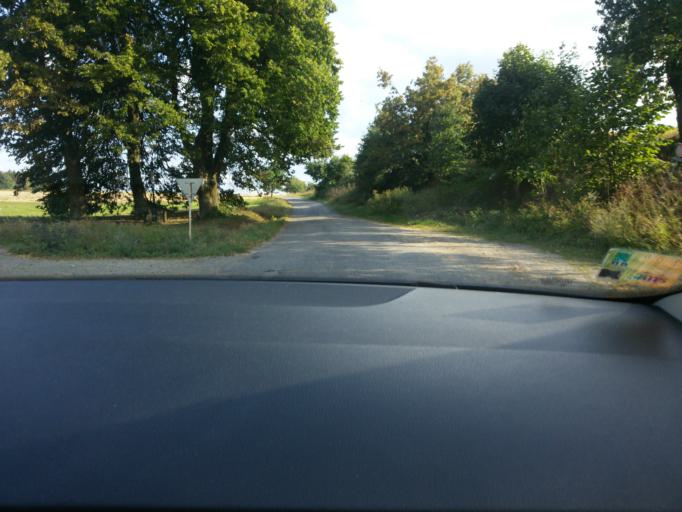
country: CZ
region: South Moravian
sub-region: Okres Brno-Venkov
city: Lomnice
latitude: 49.4796
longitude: 16.4274
